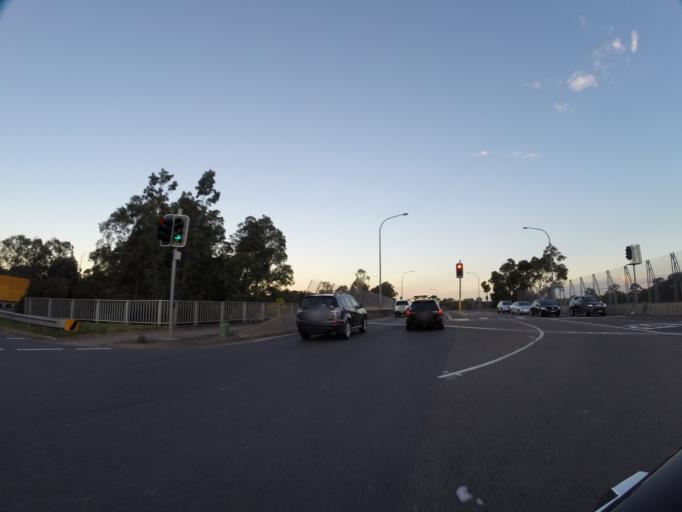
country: AU
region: New South Wales
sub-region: Bankstown
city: Milperra
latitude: -33.9417
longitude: 150.9422
